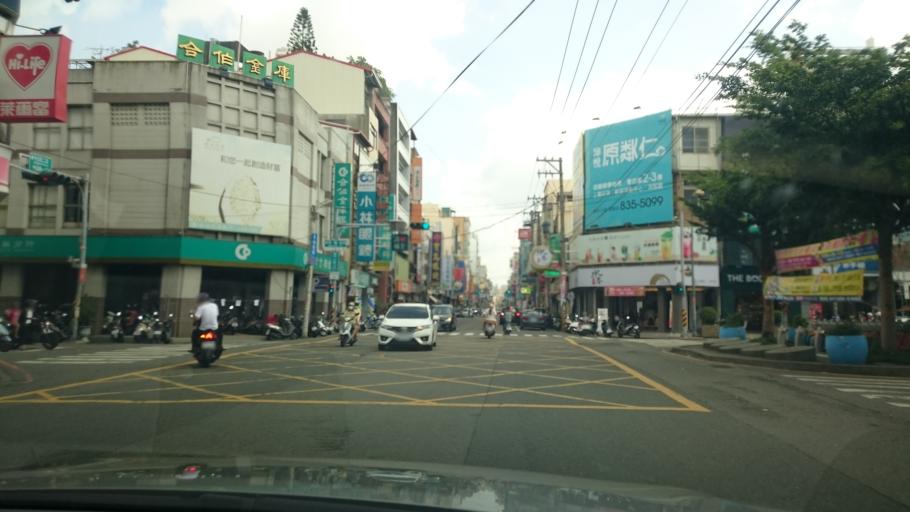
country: TW
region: Taiwan
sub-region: Nantou
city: Nantou
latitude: 23.9596
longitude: 120.5707
